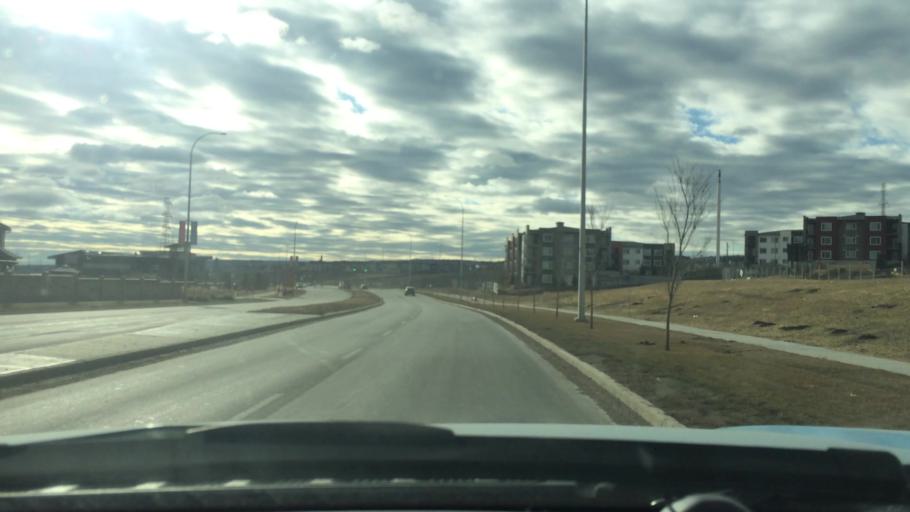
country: CA
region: Alberta
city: Calgary
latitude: 51.1722
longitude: -114.1340
